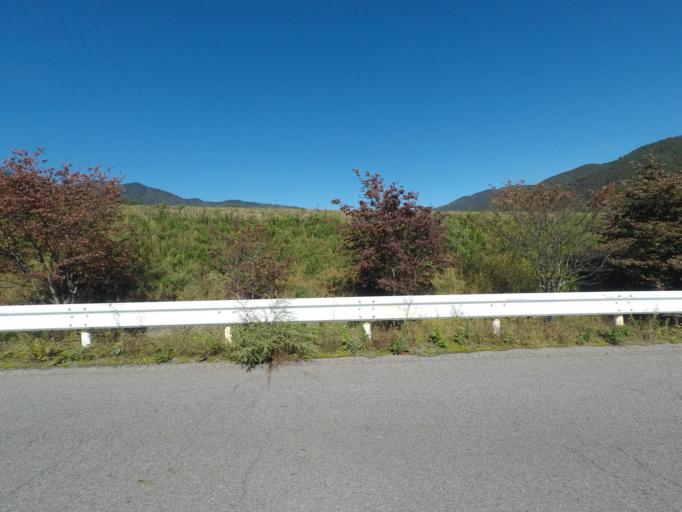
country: JP
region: Nagano
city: Tatsuno
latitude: 35.9756
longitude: 137.7440
